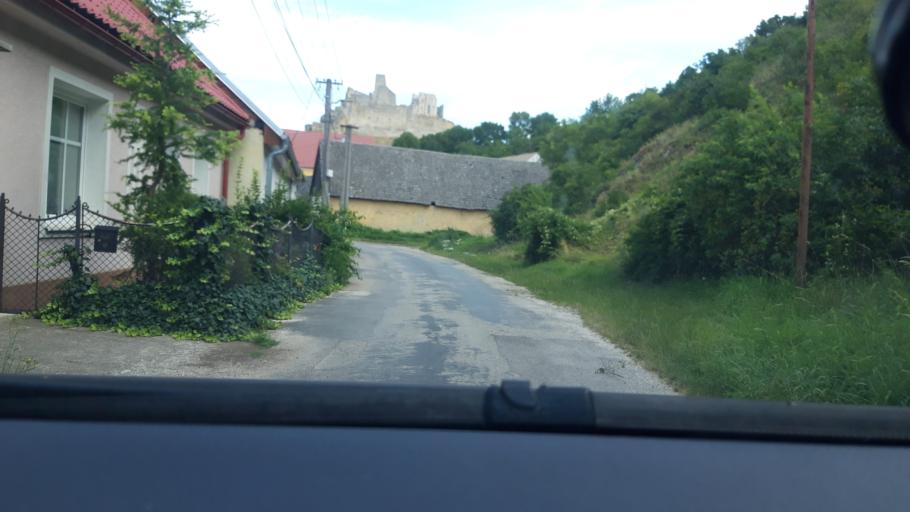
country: SK
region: Trenciansky
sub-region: Okres Nove Mesto nad Vahom
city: Nove Mesto nad Vahom
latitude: 48.7876
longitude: 17.8981
